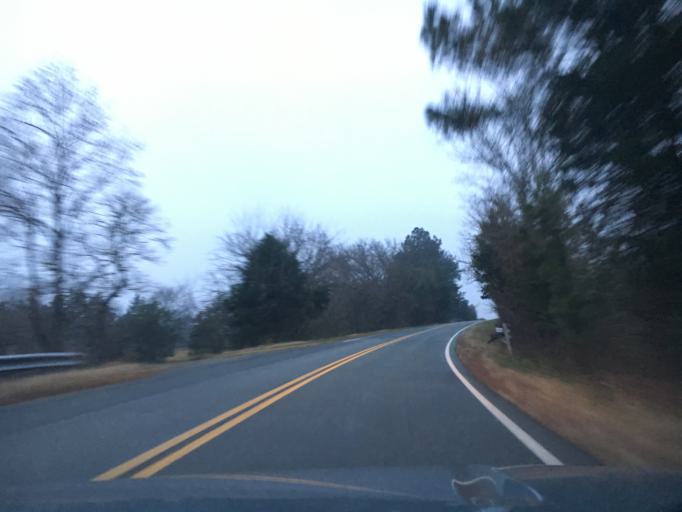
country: US
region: Virginia
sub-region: Halifax County
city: South Boston
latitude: 36.6990
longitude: -78.9656
